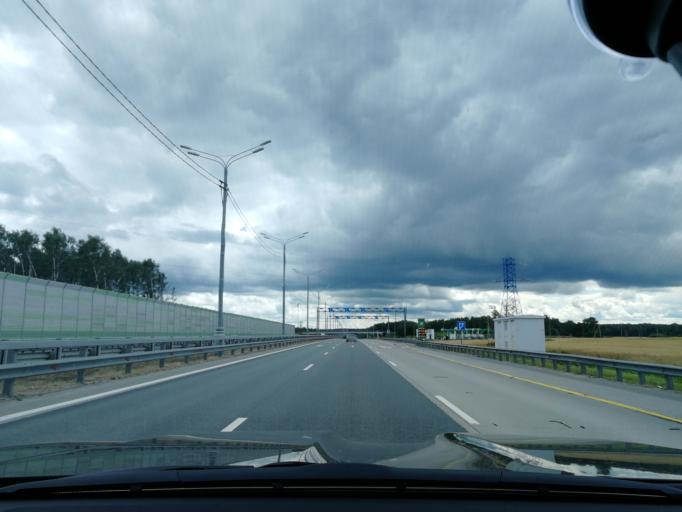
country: RU
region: Moskovskaya
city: Barybino
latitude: 55.2614
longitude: 37.8672
